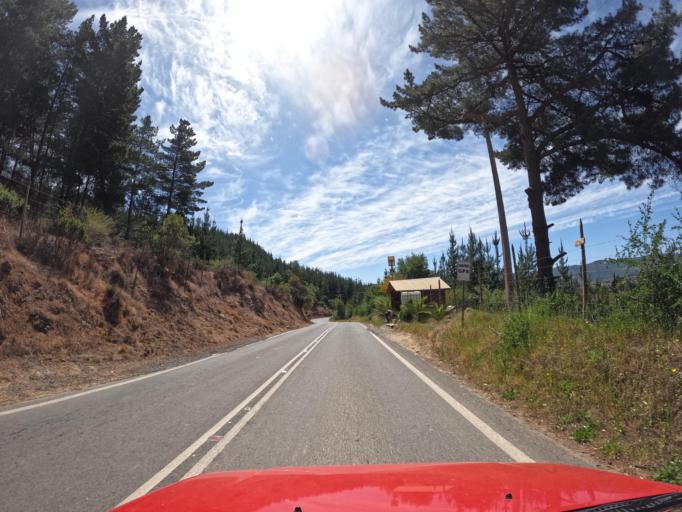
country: CL
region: Maule
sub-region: Provincia de Talca
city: Talca
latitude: -34.9926
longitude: -71.8097
